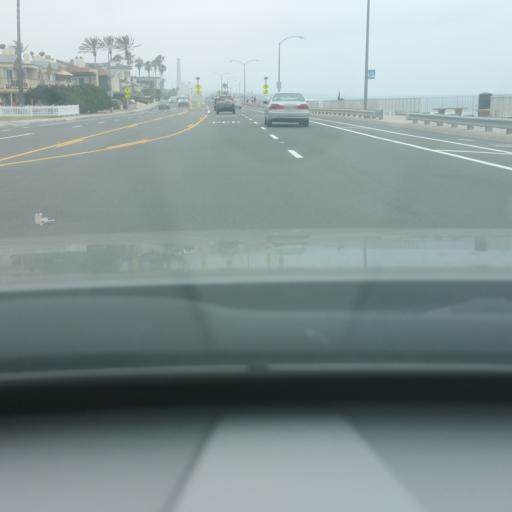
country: US
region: California
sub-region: San Diego County
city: Carlsbad
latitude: 33.1528
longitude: -117.3495
